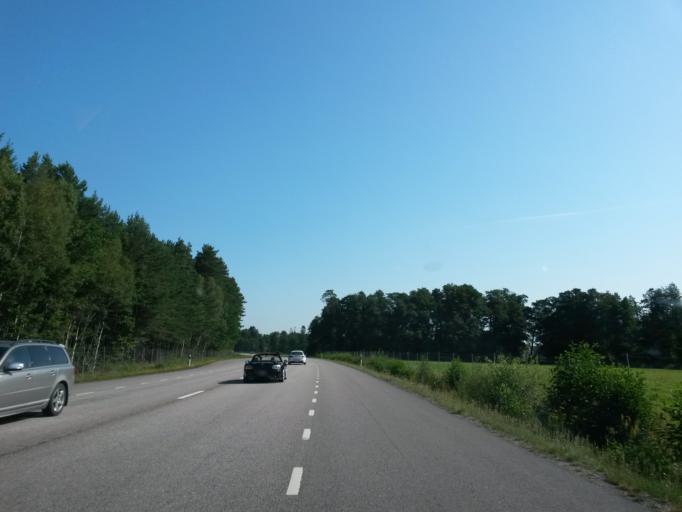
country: SE
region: Vaestra Goetaland
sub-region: Vara Kommun
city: Vara
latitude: 58.2246
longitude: 12.9217
